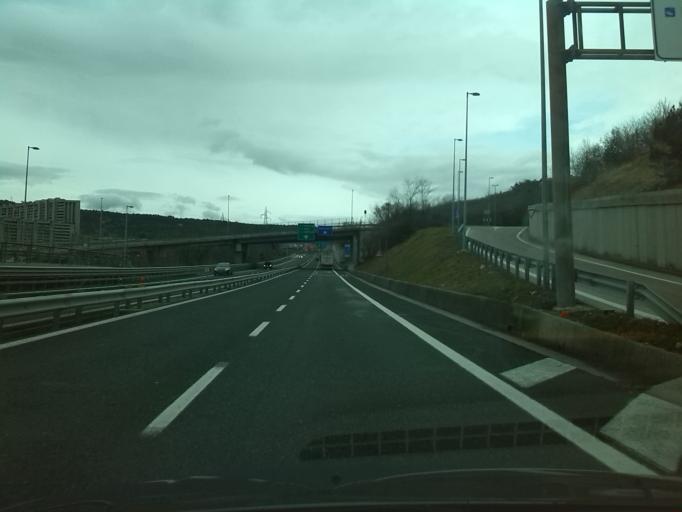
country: IT
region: Friuli Venezia Giulia
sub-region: Provincia di Trieste
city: Trieste
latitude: 45.6371
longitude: 13.8157
